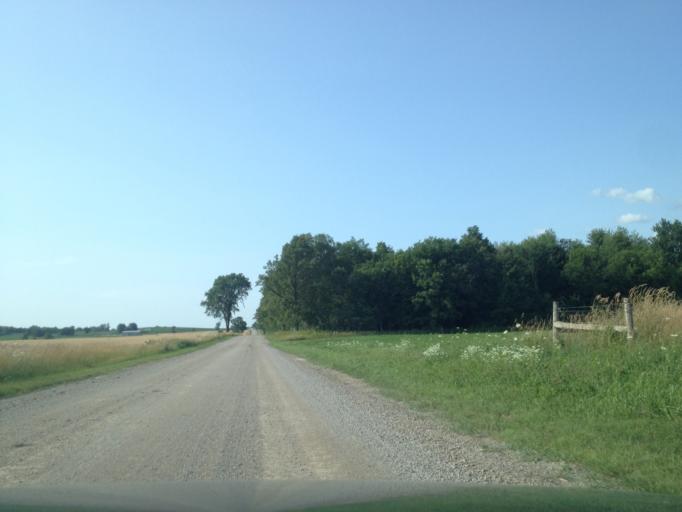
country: CA
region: Ontario
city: Ingersoll
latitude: 42.9497
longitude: -80.7719
